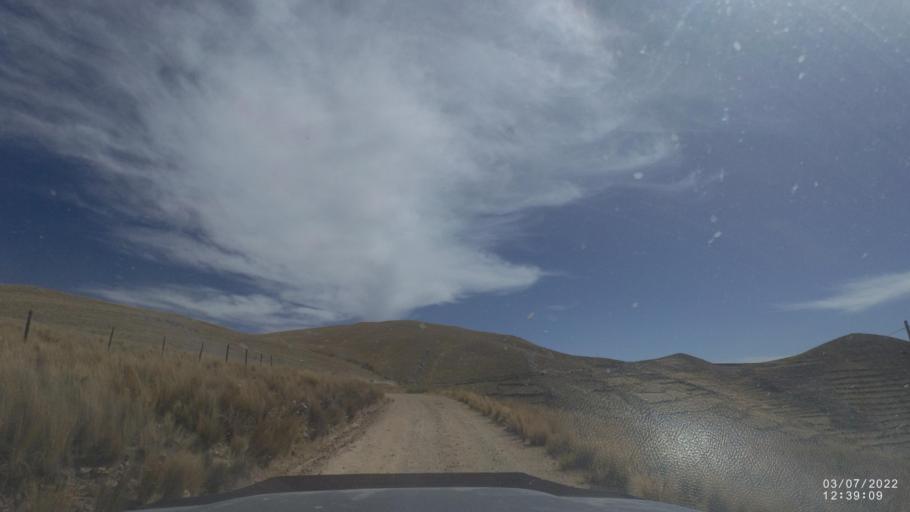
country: BO
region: Cochabamba
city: Irpa Irpa
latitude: -17.7889
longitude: -66.6221
